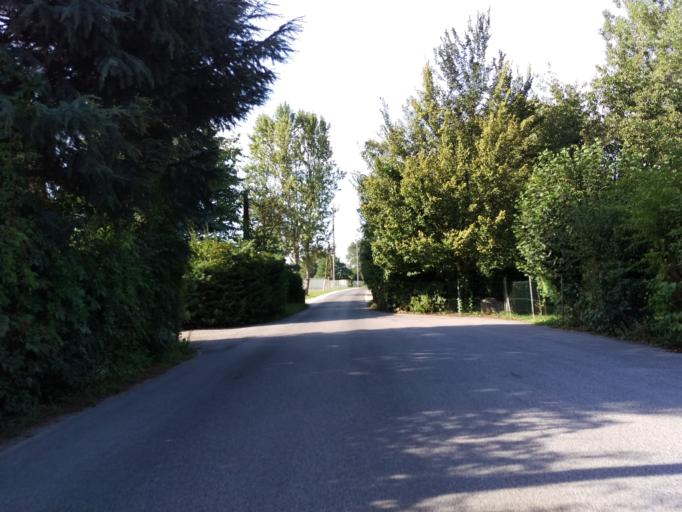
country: AT
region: Styria
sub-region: Politischer Bezirk Graz-Umgebung
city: Feldkirchen bei Graz
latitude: 47.0389
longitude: 15.4423
